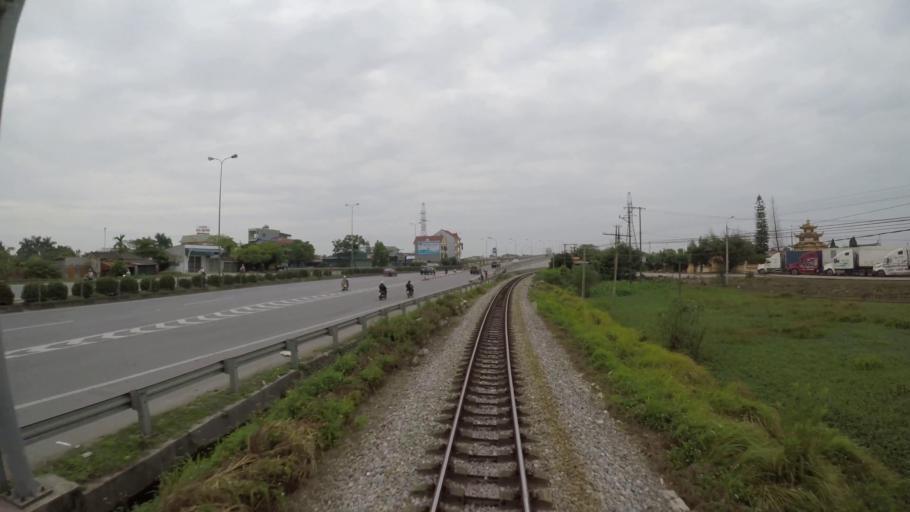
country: VN
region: Hai Duong
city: Thanh Pho Hai Duong
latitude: 20.9634
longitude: 106.3738
